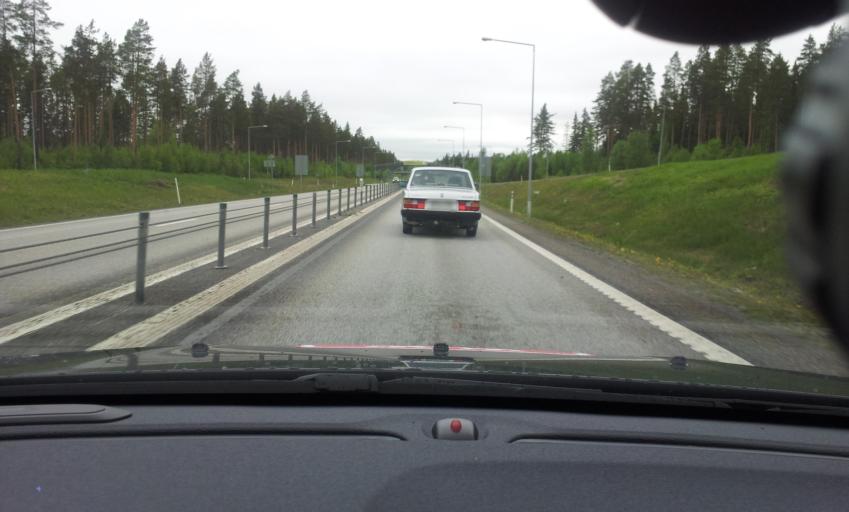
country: SE
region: Jaemtland
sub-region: OEstersunds Kommun
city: Ostersund
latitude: 63.2032
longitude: 14.6771
